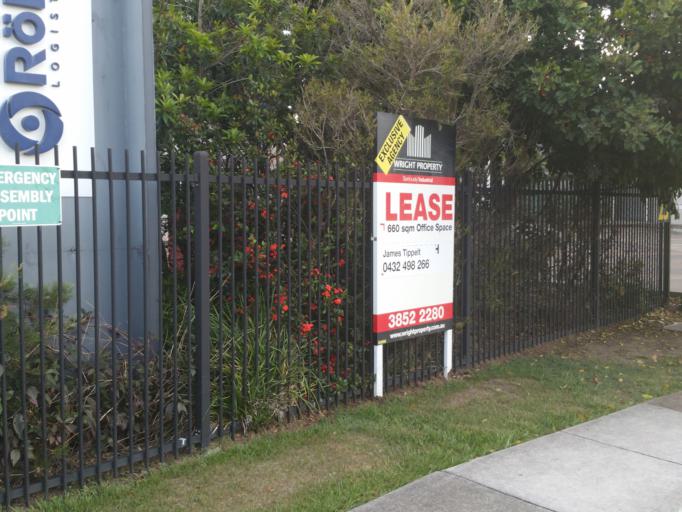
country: AU
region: Queensland
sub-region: Brisbane
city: Ascot
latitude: -27.4155
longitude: 153.0755
